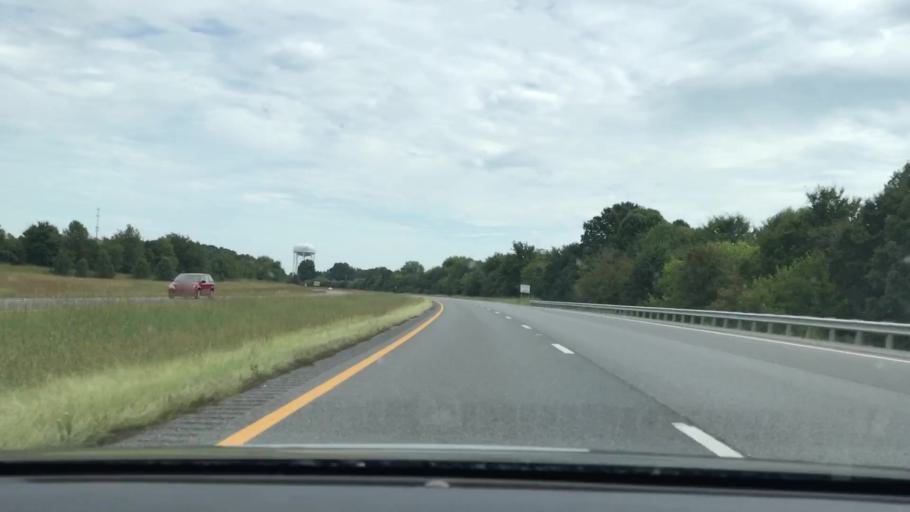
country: US
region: Kentucky
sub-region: Marshall County
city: Benton
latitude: 36.8495
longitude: -88.3750
